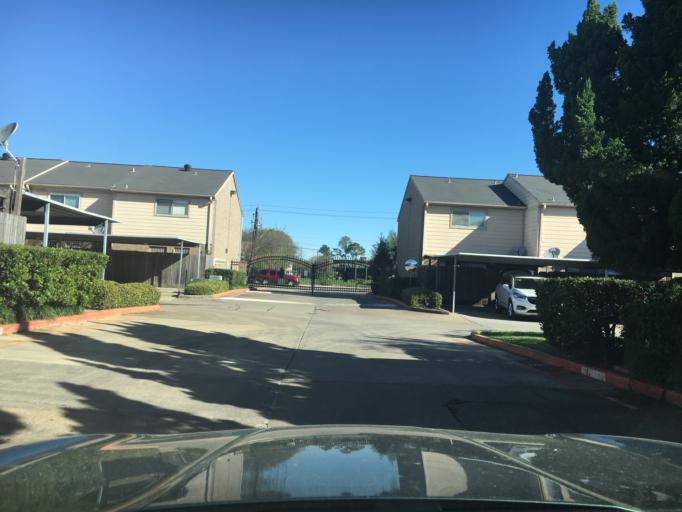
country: US
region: Texas
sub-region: Harris County
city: Bellaire
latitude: 29.7301
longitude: -95.4886
